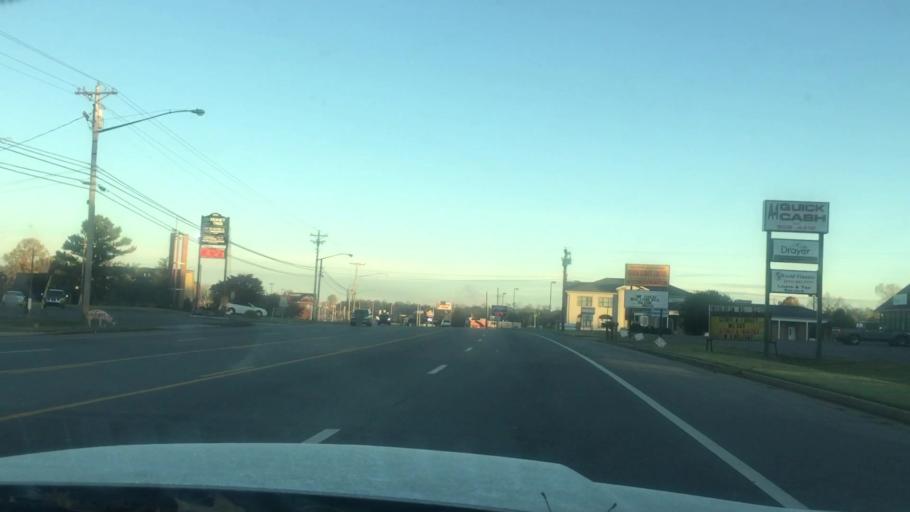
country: US
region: Tennessee
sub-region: Franklin County
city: Decherd
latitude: 35.2068
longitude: -86.0939
